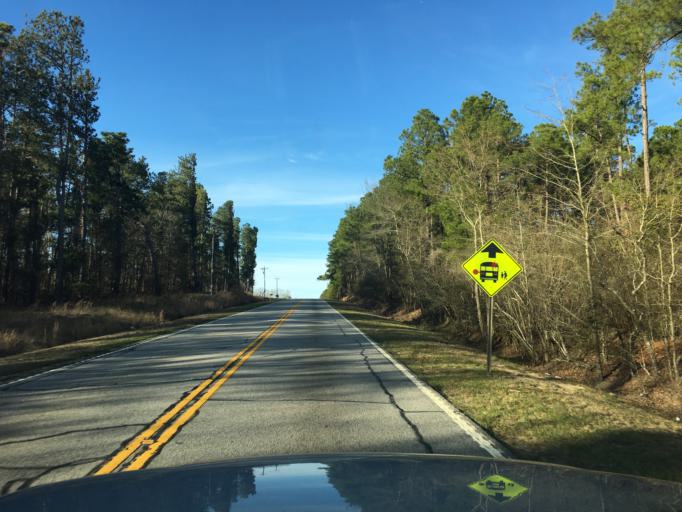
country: US
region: South Carolina
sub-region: Edgefield County
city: Johnston
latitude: 33.7489
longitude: -81.6436
